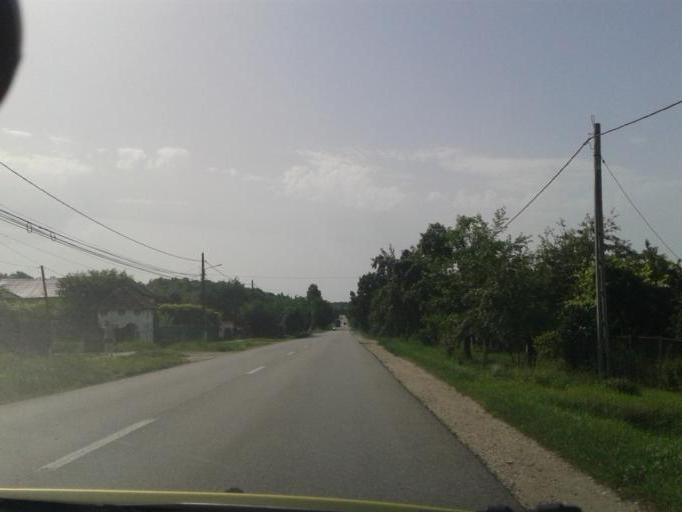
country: RO
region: Valcea
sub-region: Oras Baile Govora
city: Baile Govora
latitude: 45.0972
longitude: 24.2099
